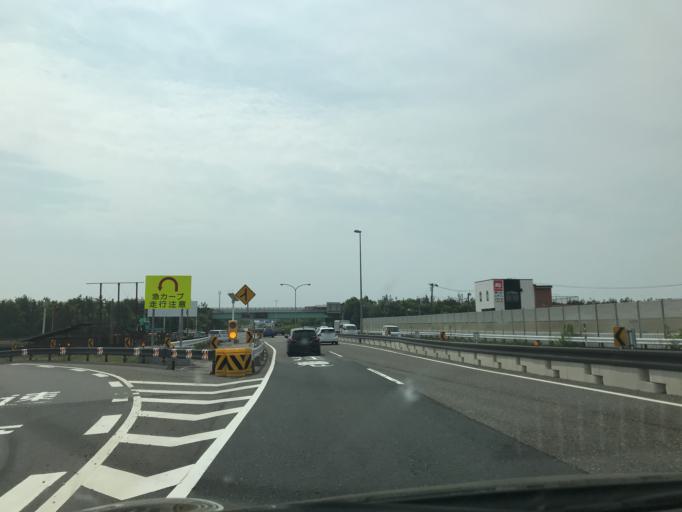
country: JP
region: Niigata
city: Kameda-honcho
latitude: 37.8829
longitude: 139.0803
